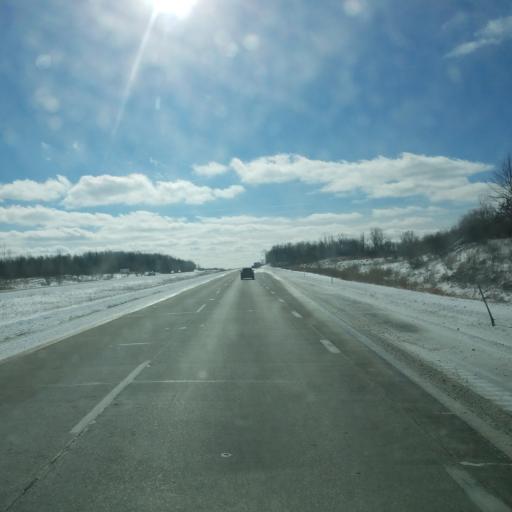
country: US
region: Michigan
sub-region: Clinton County
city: DeWitt
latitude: 42.9059
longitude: -84.5178
